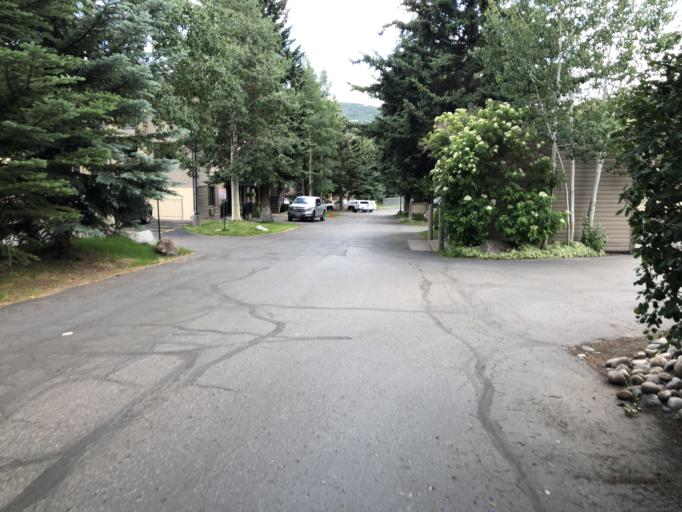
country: US
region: Colorado
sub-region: Eagle County
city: Avon
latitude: 39.6385
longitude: -106.5264
